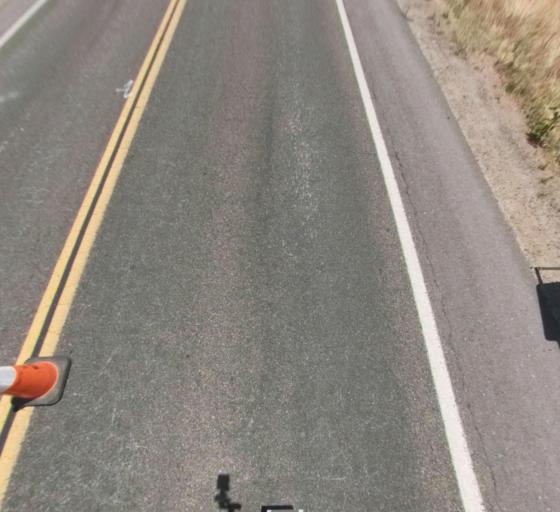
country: US
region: California
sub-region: Madera County
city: Bonadelle Ranchos-Madera Ranchos
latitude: 36.9666
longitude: -119.8837
